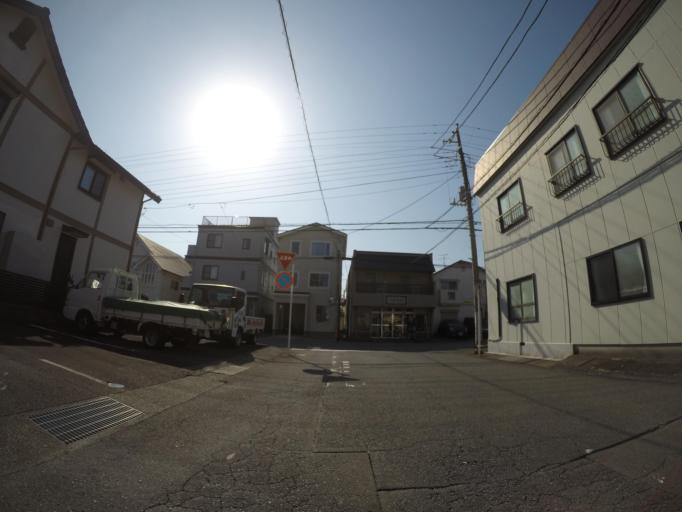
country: JP
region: Shizuoka
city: Numazu
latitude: 35.1021
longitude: 138.8501
